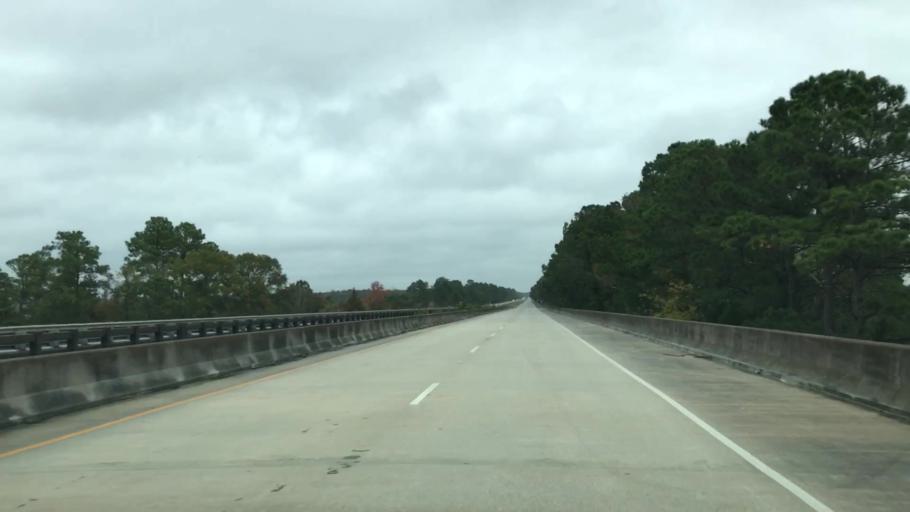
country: US
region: South Carolina
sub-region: Georgetown County
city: Georgetown
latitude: 33.1852
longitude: -79.4046
